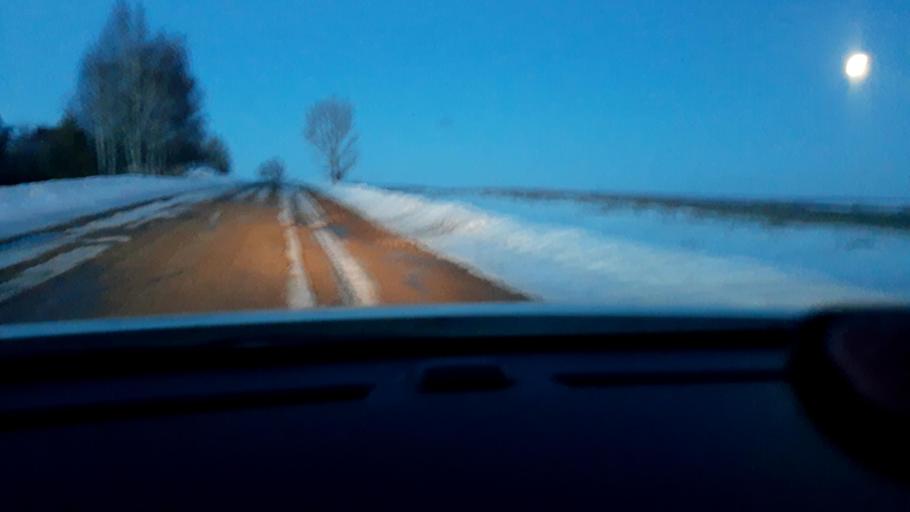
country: RU
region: Bashkortostan
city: Avdon
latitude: 54.3953
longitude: 55.7002
